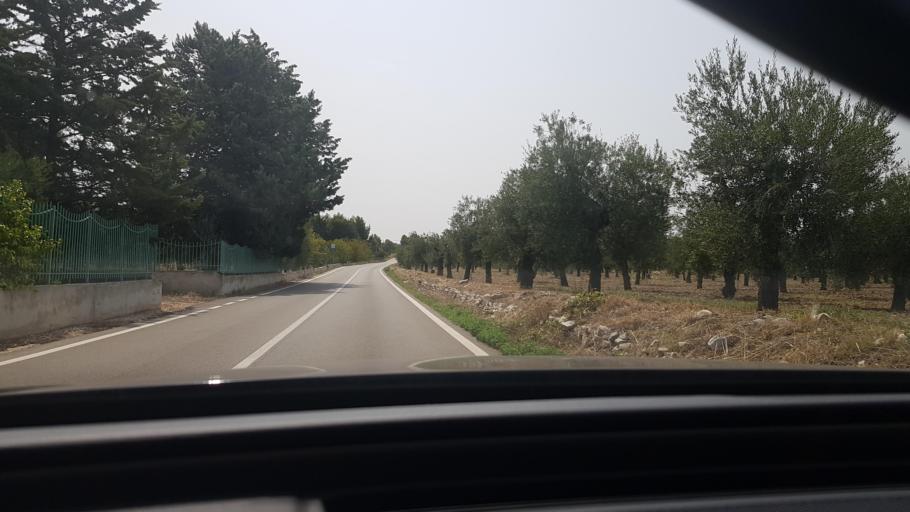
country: IT
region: Apulia
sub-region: Provincia di Barletta - Andria - Trani
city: Andria
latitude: 41.1095
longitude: 16.2806
